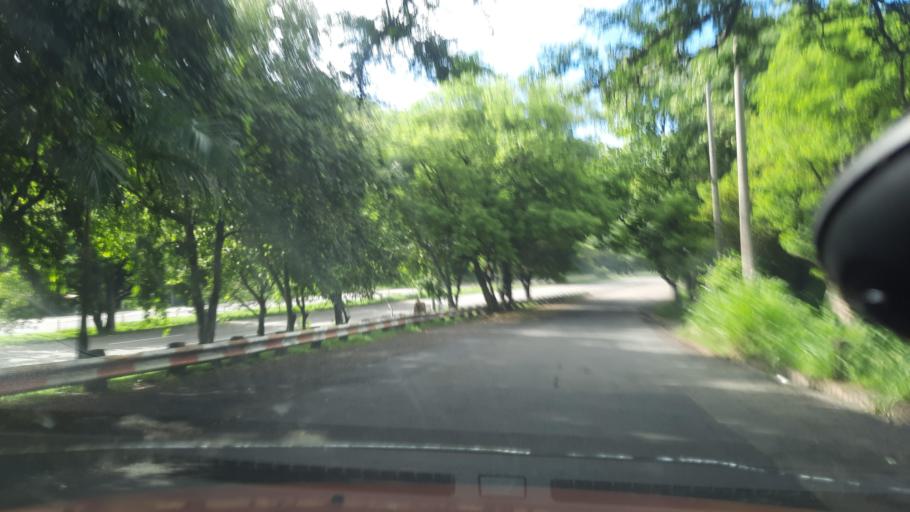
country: SV
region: La Paz
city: Olocuilta
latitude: 13.5628
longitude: -89.1159
